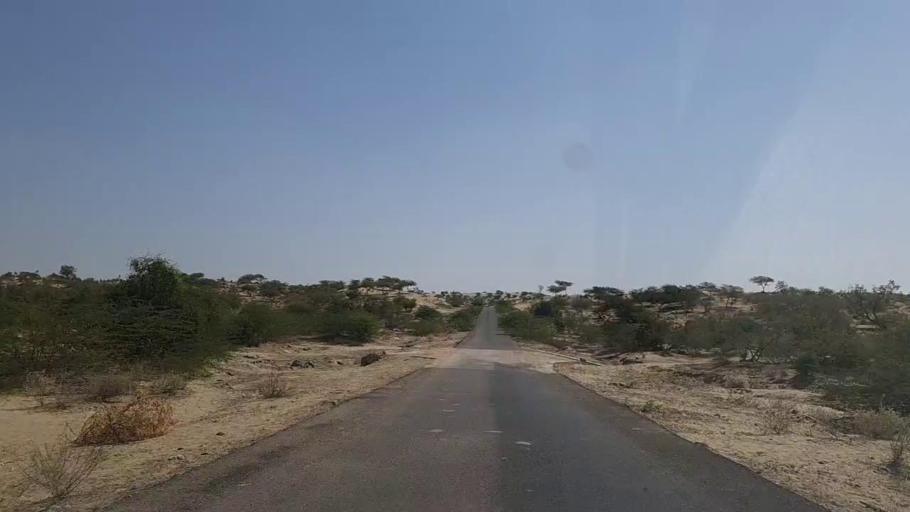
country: PK
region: Sindh
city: Diplo
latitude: 24.4860
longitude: 69.4480
